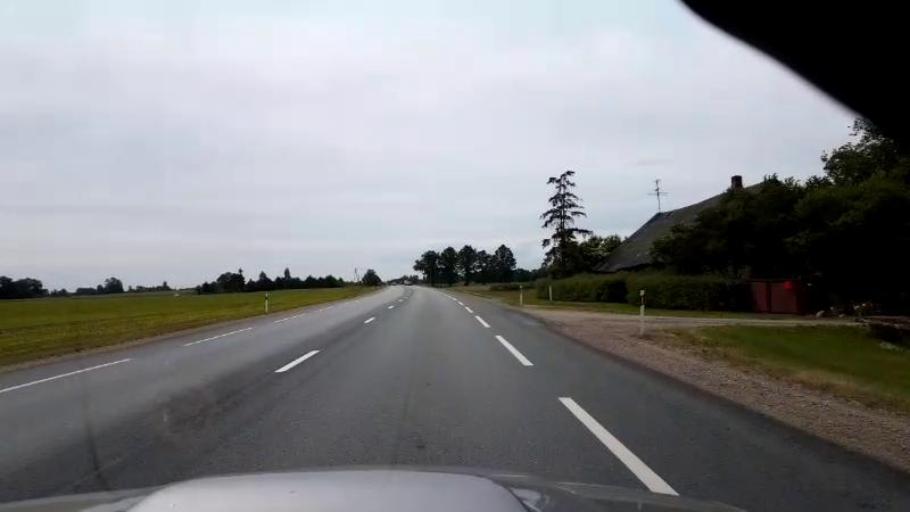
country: LV
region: Lecava
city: Iecava
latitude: 56.5742
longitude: 24.1770
